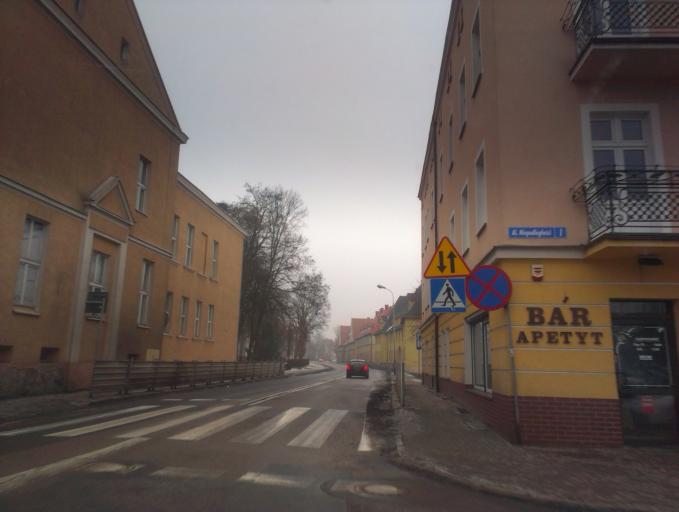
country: PL
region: Greater Poland Voivodeship
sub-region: Powiat pilski
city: Pila
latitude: 53.1530
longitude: 16.7374
